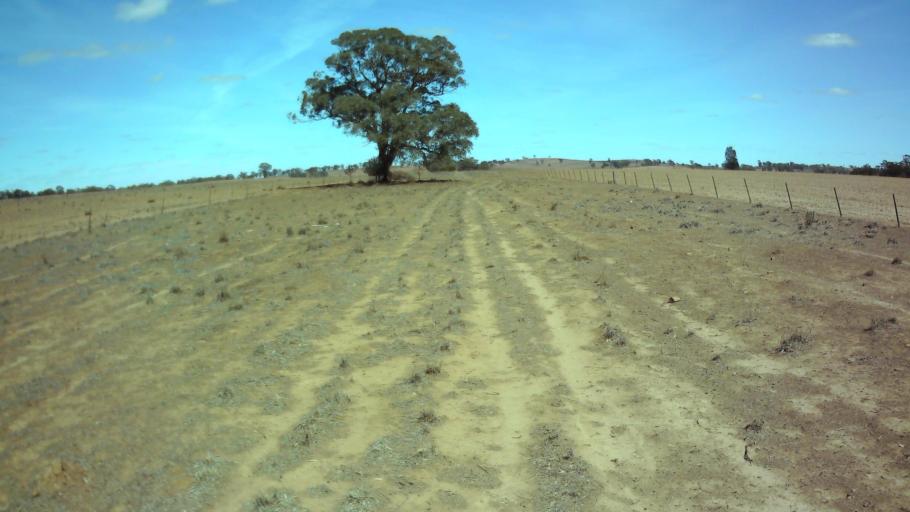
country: AU
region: New South Wales
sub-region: Weddin
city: Grenfell
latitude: -33.7229
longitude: 147.8563
